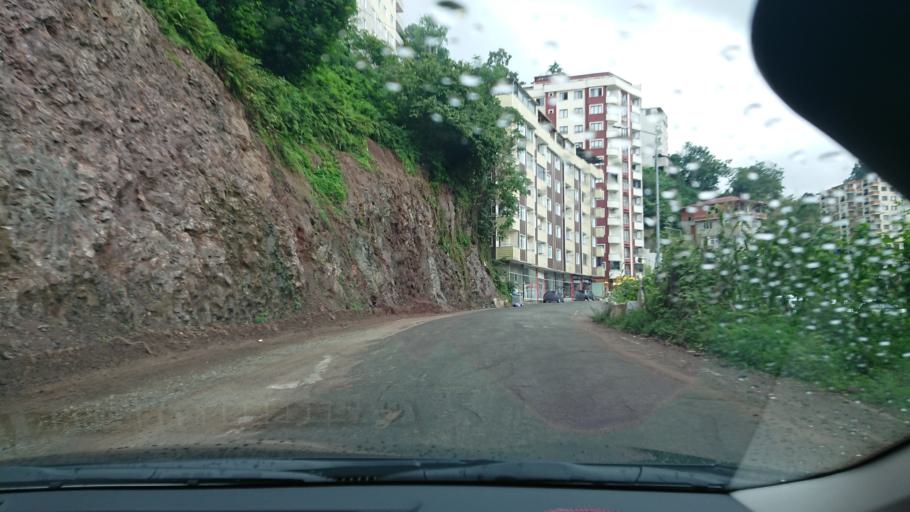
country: TR
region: Rize
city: Rize
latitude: 41.0249
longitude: 40.5128
